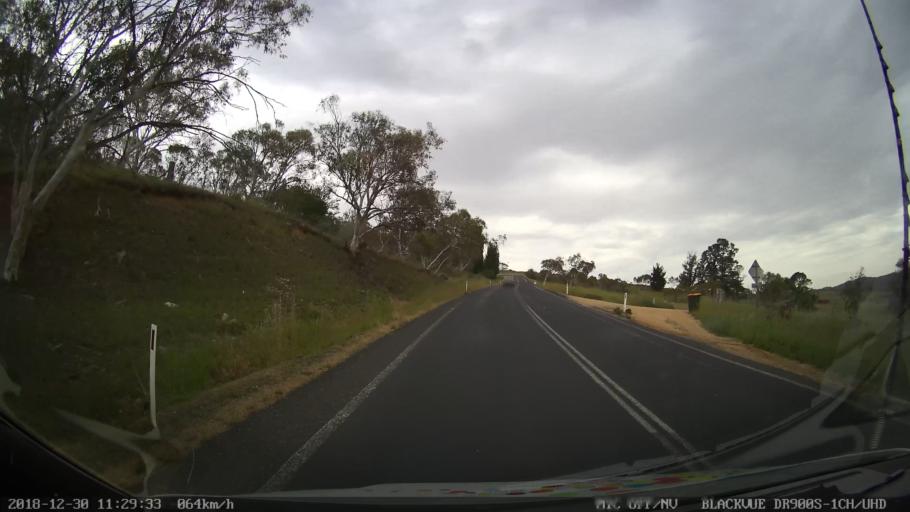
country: AU
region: New South Wales
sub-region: Snowy River
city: Jindabyne
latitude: -36.4496
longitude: 148.6097
